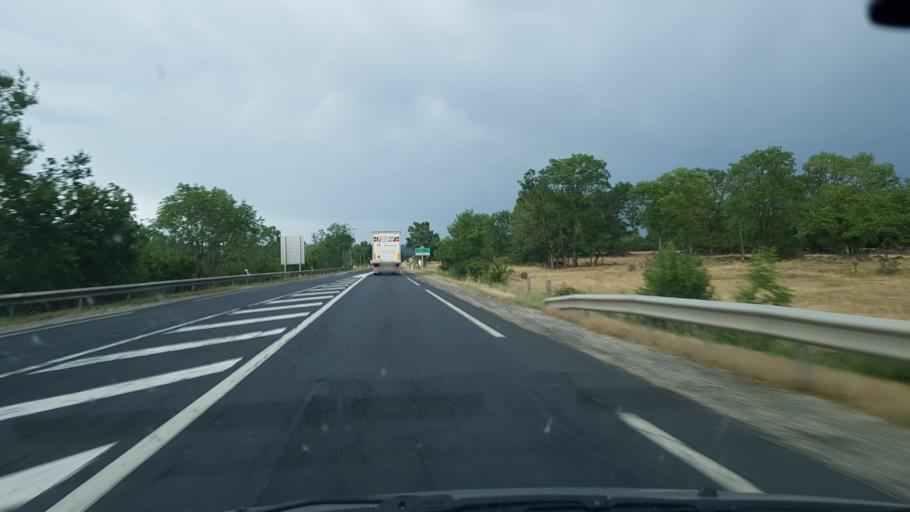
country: FR
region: Auvergne
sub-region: Departement de la Haute-Loire
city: Langeac
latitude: 45.1424
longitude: 3.5652
